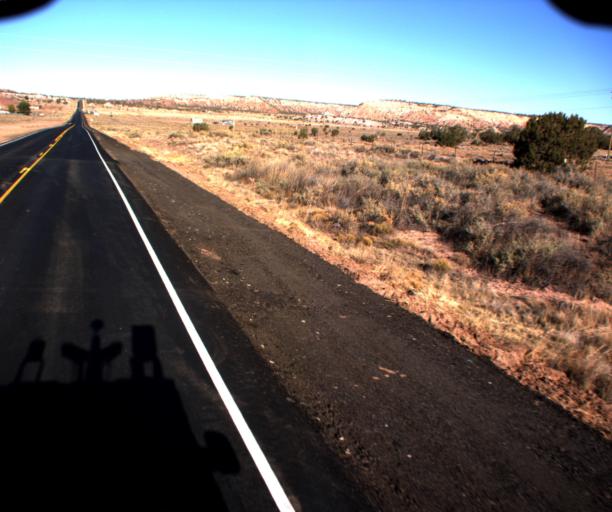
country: US
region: Arizona
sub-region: Apache County
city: Ganado
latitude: 35.7211
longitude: -109.5758
